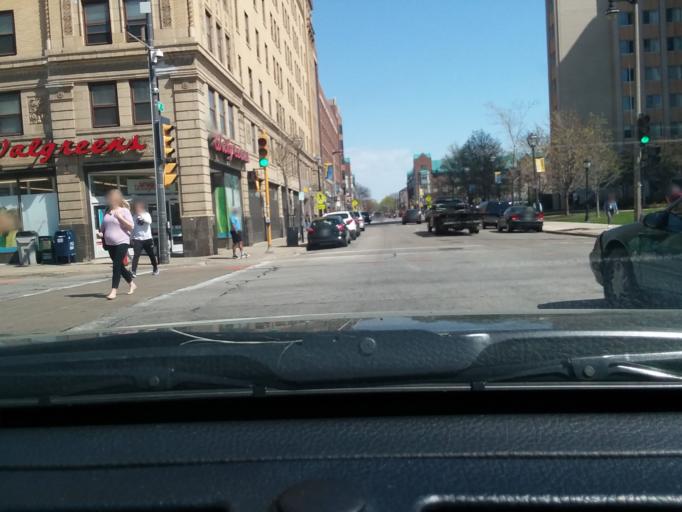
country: US
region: Wisconsin
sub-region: Milwaukee County
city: Milwaukee
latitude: 43.0386
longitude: -87.9330
